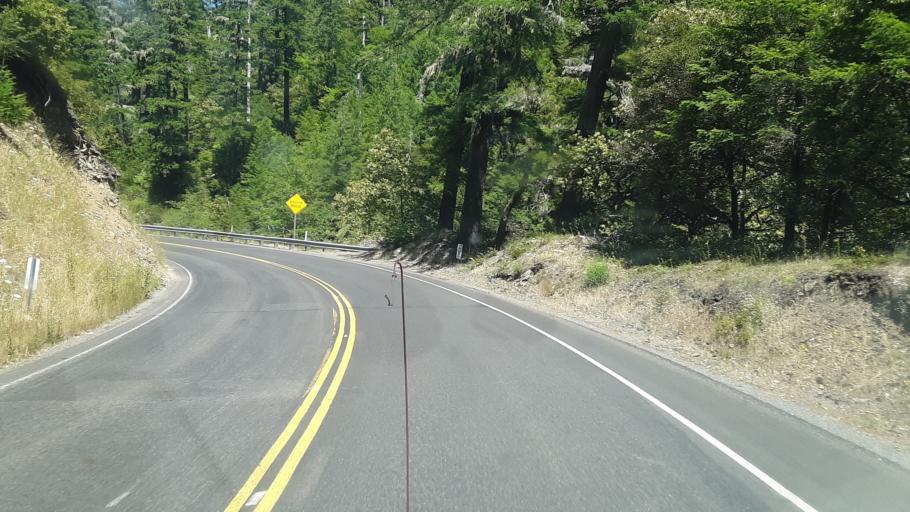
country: US
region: Oregon
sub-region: Josephine County
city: Cave Junction
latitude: 41.8784
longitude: -123.8275
